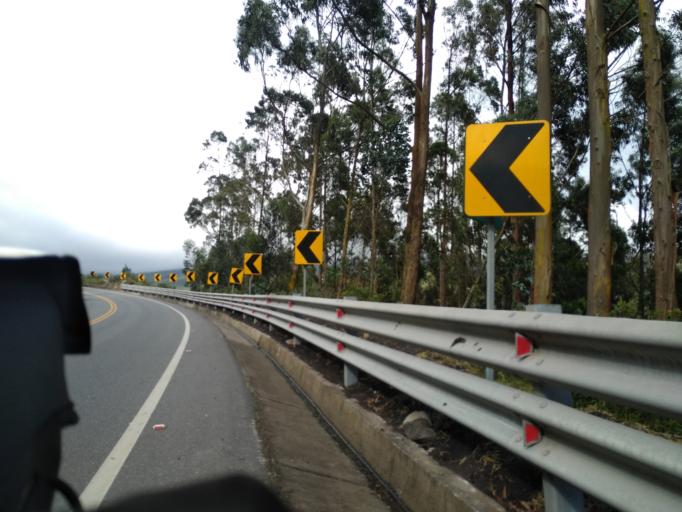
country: EC
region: Tungurahua
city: Banos
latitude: -1.4931
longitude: -78.5189
